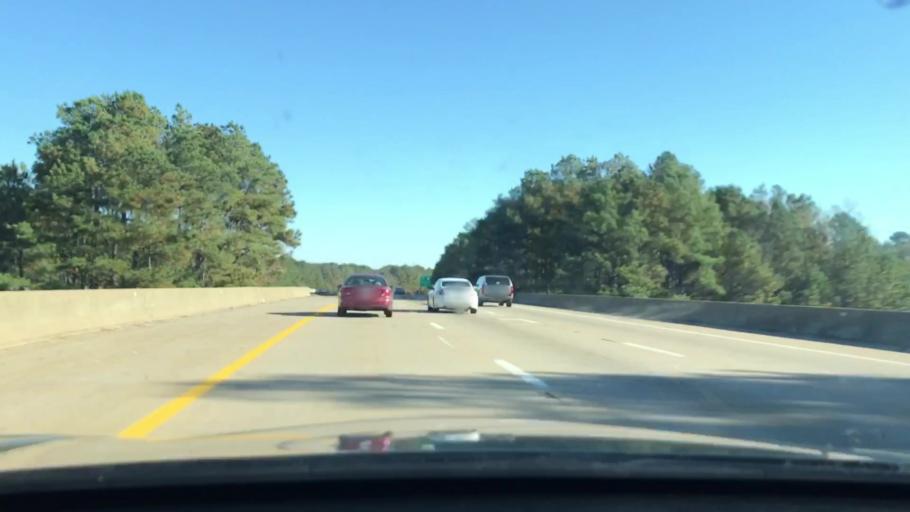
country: US
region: Virginia
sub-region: Henrico County
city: Glen Allen
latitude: 37.6766
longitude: -77.5034
